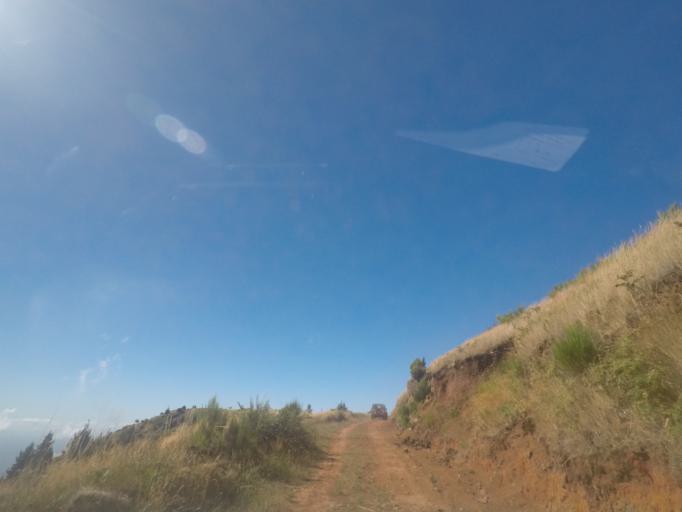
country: PT
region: Madeira
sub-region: Funchal
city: Nossa Senhora do Monte
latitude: 32.7046
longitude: -16.9063
